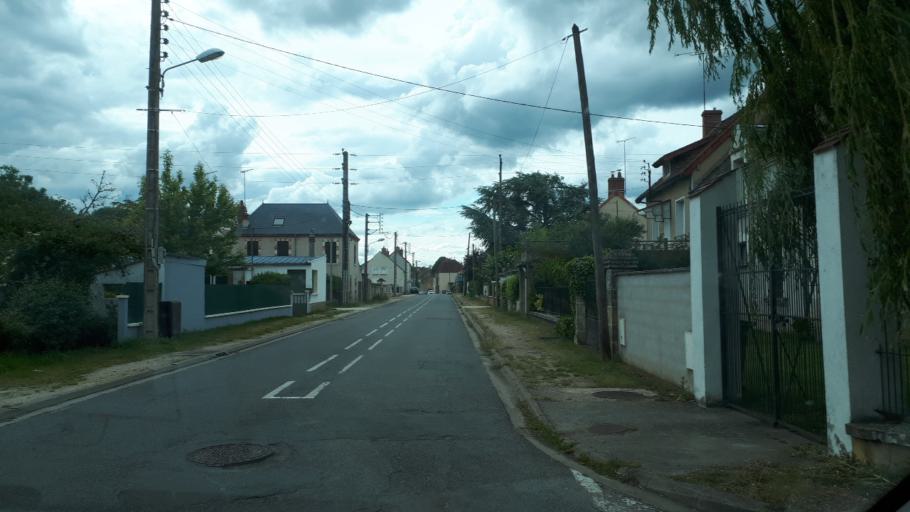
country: FR
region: Centre
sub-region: Departement du Cher
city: Gracay
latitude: 47.1423
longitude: 1.8535
